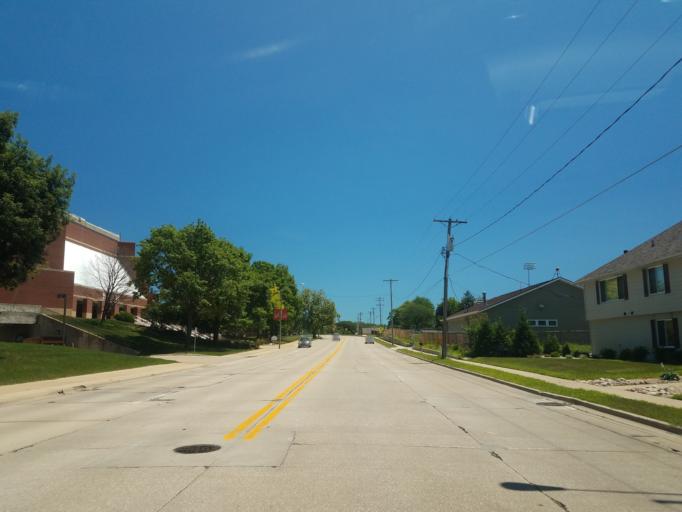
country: US
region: Illinois
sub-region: McLean County
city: Normal
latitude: 40.5099
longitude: -88.9996
